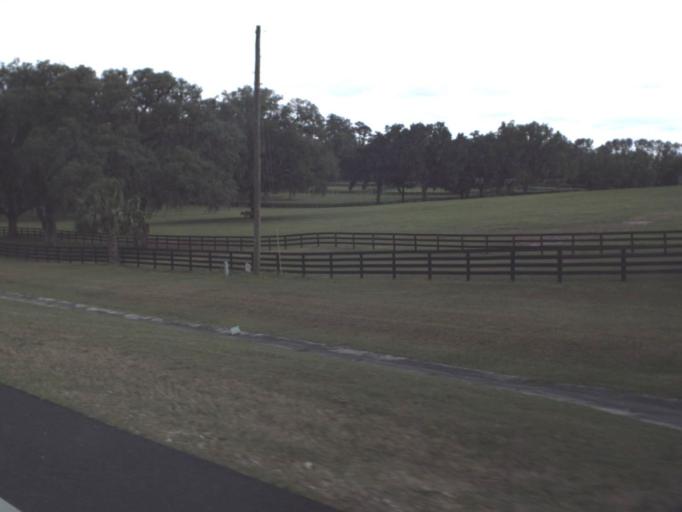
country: US
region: Florida
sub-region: Marion County
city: Ocala
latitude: 29.2436
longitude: -82.2860
